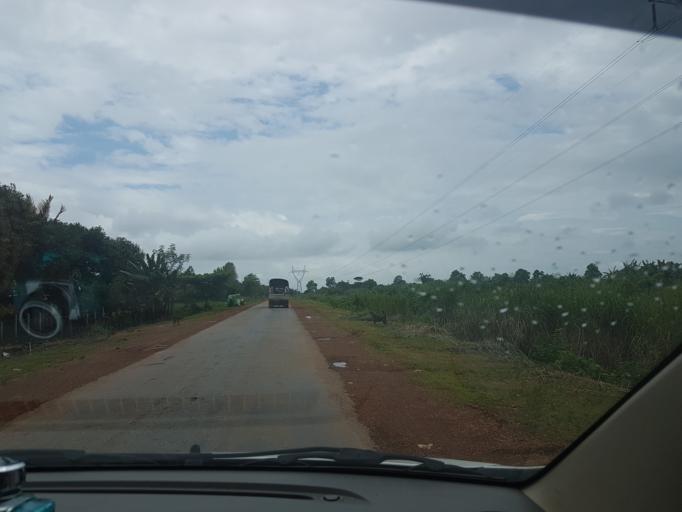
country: MM
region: Bago
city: Nyaunglebin
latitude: 17.9302
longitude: 96.8166
